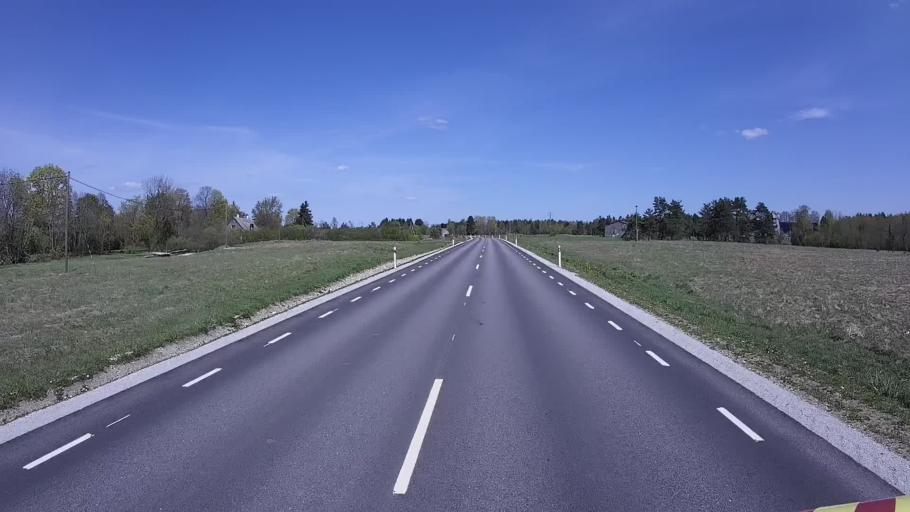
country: EE
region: Harju
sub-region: Nissi vald
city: Turba
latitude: 59.1799
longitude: 24.0832
